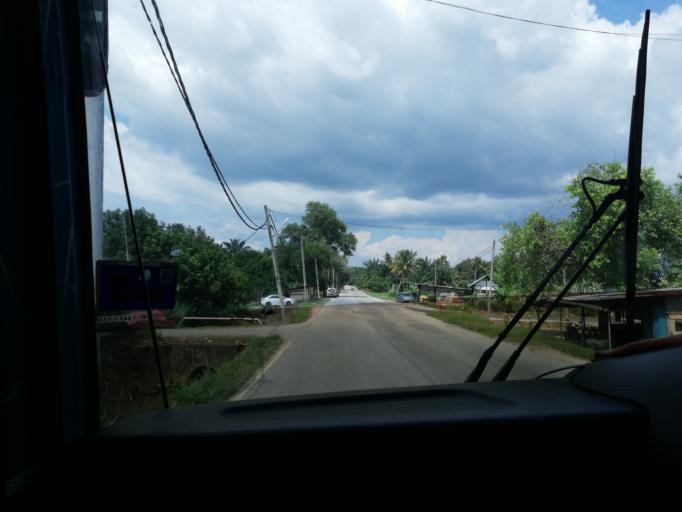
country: MY
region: Perak
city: Parit Buntar
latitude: 5.1187
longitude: 100.5622
